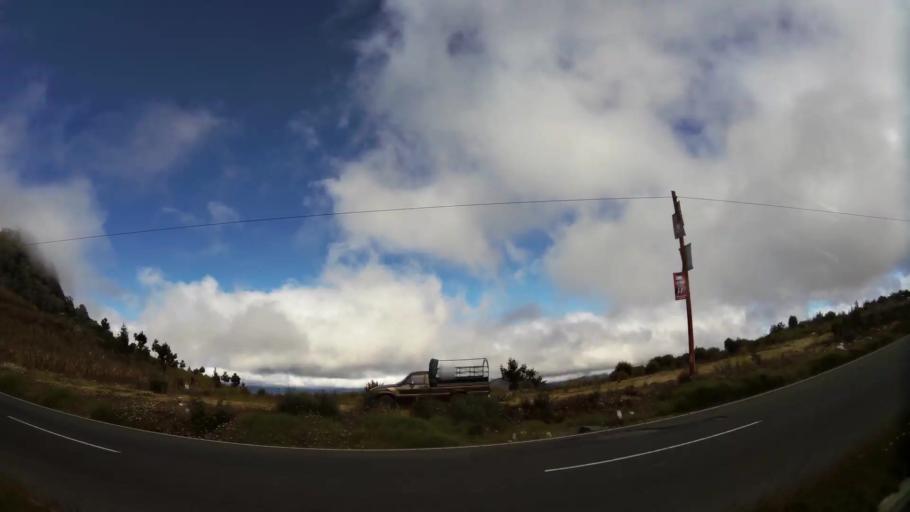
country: GT
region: Solola
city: Santa Catarina Ixtahuacan
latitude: 14.8424
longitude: -91.3722
